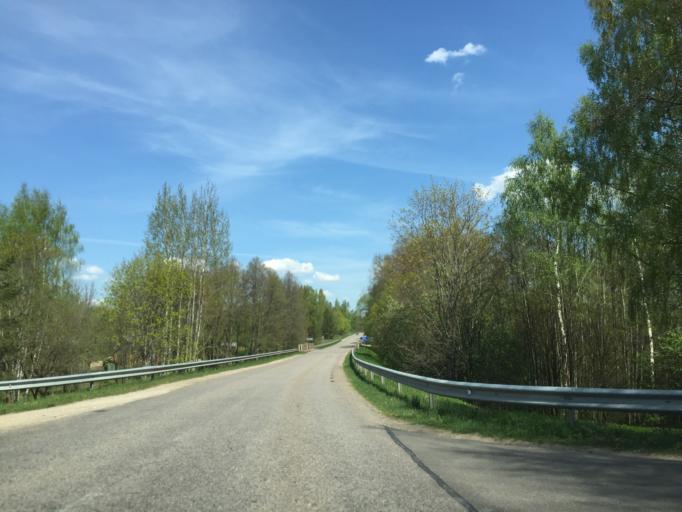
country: LV
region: Krimulda
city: Ragana
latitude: 57.3251
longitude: 24.6399
